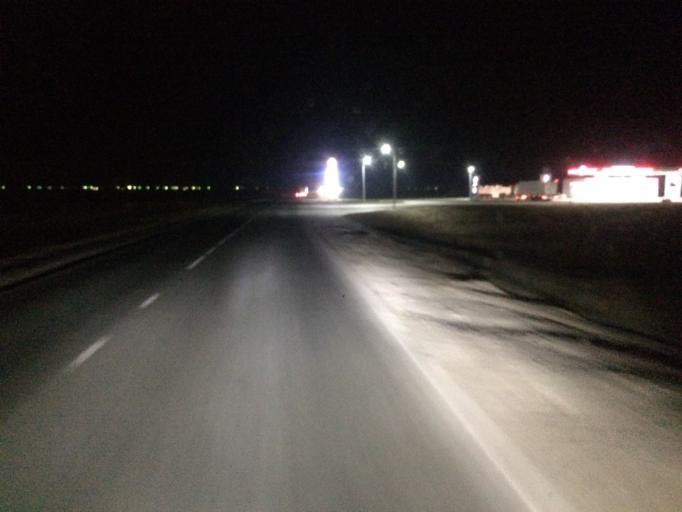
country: KZ
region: Batys Qazaqstan
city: Oral
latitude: 51.2179
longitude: 51.2776
